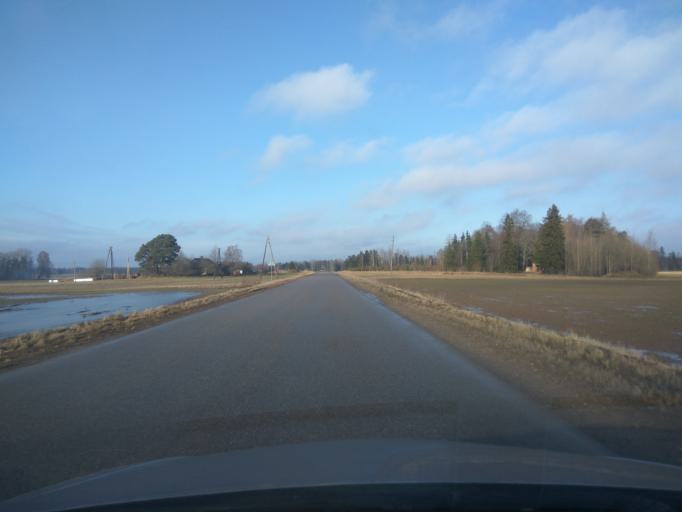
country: LV
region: Saldus Rajons
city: Saldus
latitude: 56.8240
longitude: 22.3767
